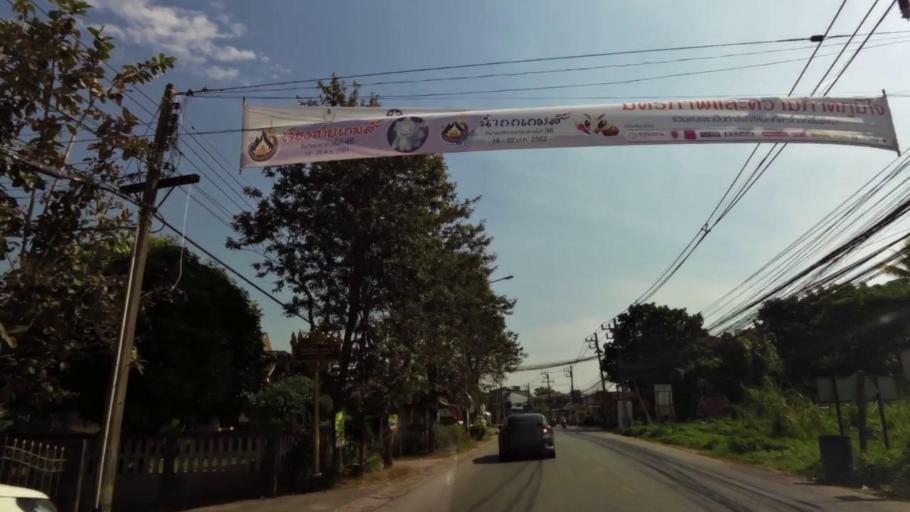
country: TH
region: Chiang Rai
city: Chiang Rai
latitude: 19.9256
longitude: 99.8376
